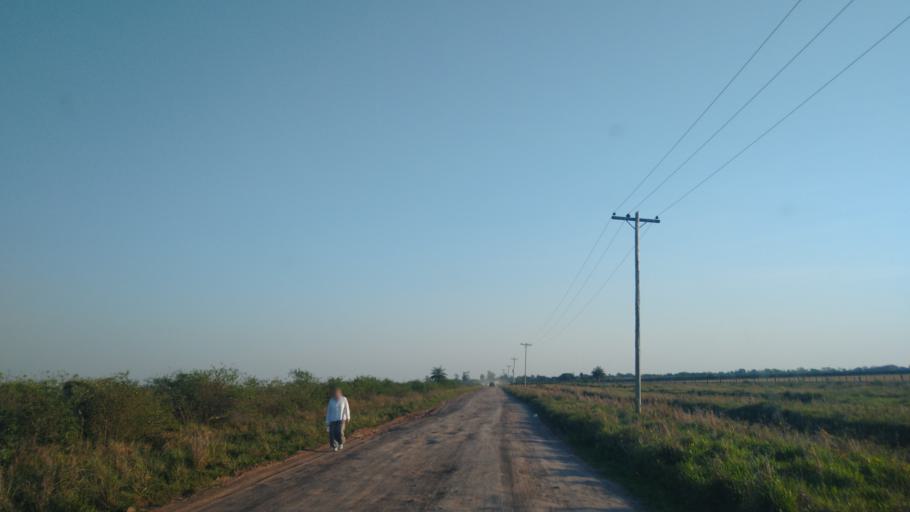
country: PY
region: Neembucu
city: Cerrito
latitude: -27.3856
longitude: -57.6574
